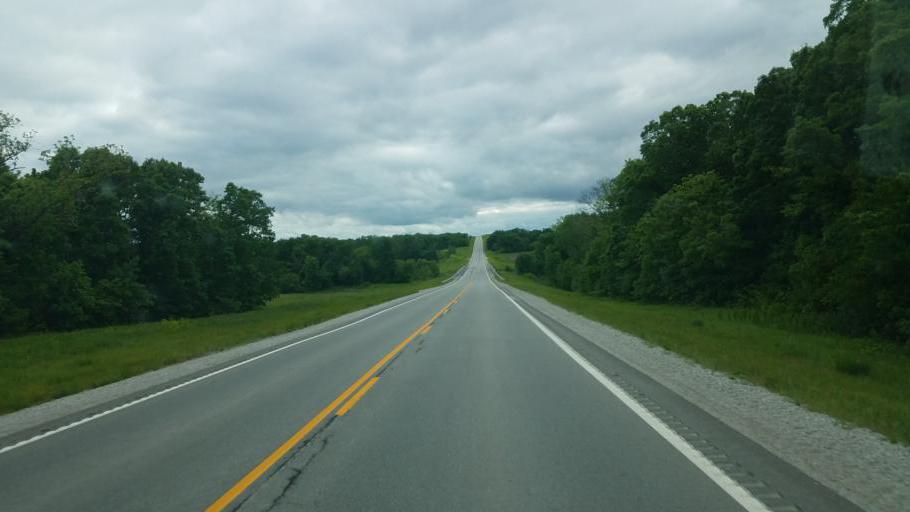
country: US
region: Missouri
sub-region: Harrison County
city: Bethany
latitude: 40.3156
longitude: -93.8067
